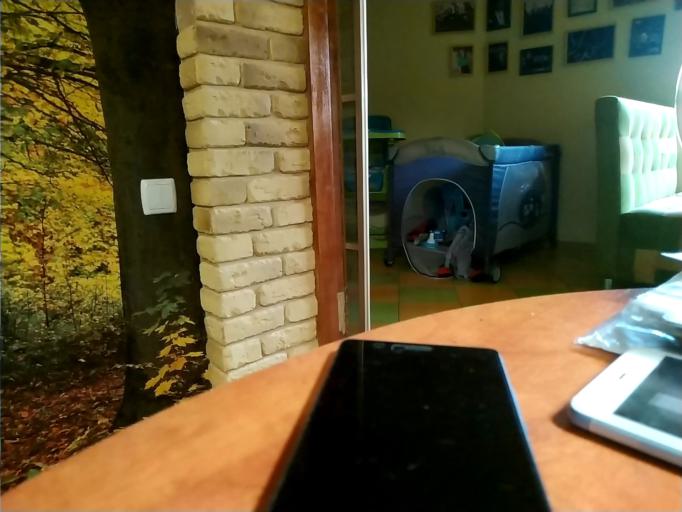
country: RU
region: Kaluga
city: Duminichi
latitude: 53.6929
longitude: 35.4341
